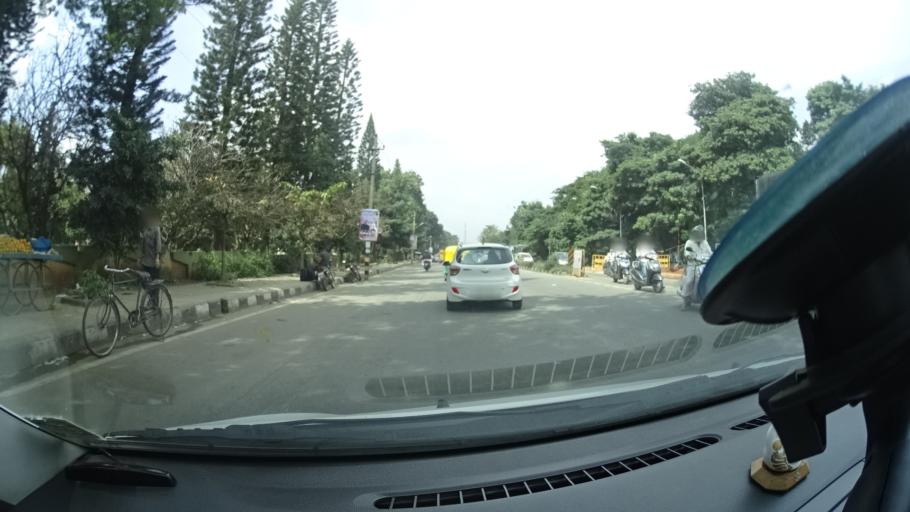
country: IN
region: Karnataka
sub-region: Bangalore Urban
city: Yelahanka
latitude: 13.1047
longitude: 77.5835
